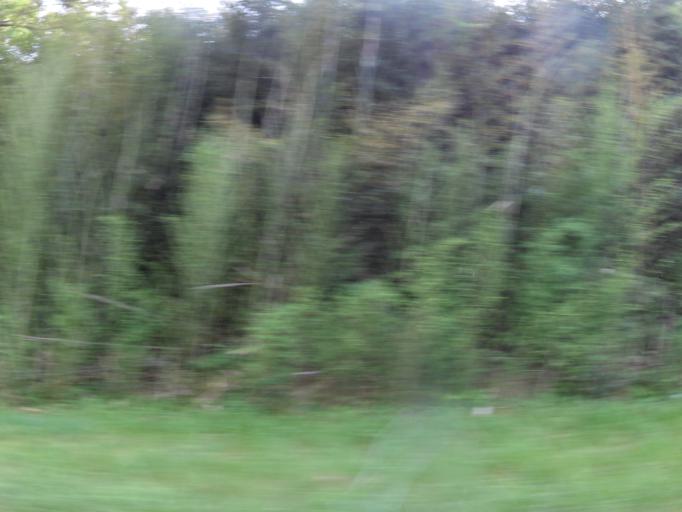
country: US
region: South Carolina
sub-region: Hampton County
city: Estill
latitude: 32.5920
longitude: -81.2071
